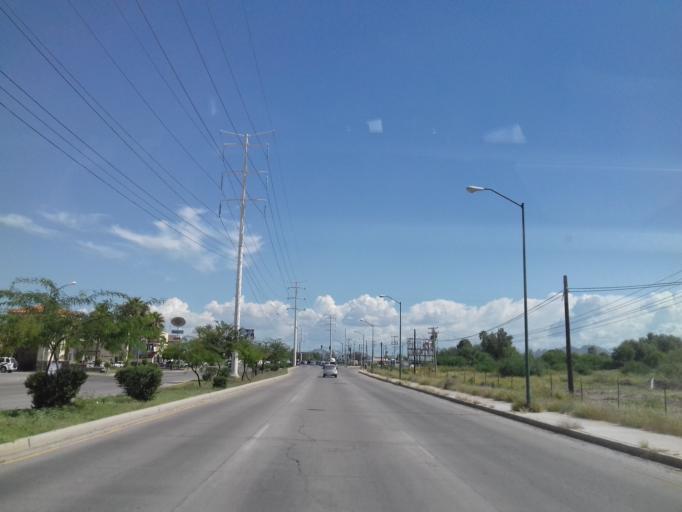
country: MX
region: Sonora
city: Hermosillo
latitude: 29.0822
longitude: -111.0084
